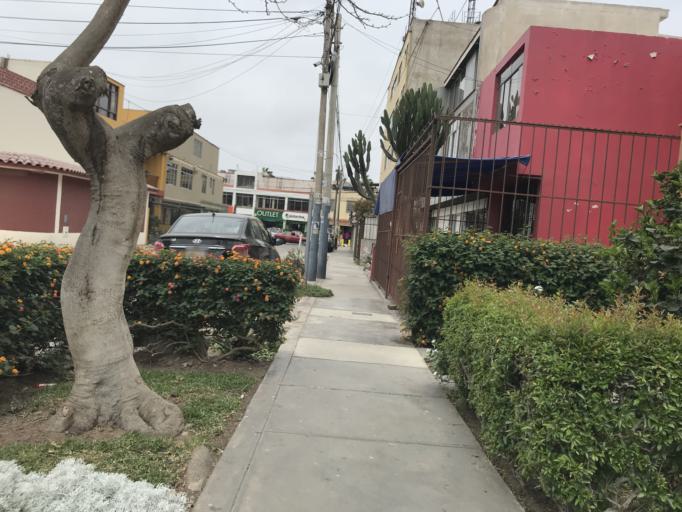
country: PE
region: Lima
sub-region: Lima
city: San Isidro
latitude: -12.0773
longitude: -77.0740
